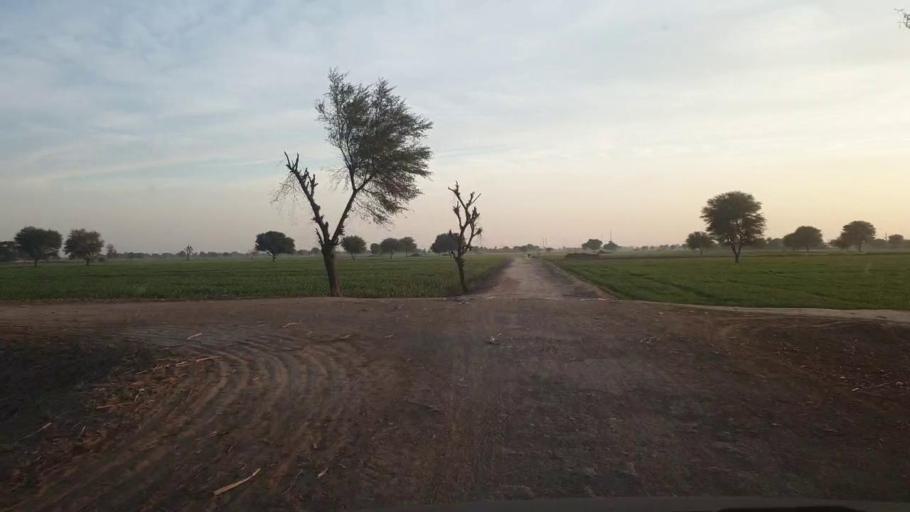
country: PK
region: Sindh
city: Shahdadpur
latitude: 26.0486
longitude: 68.5464
